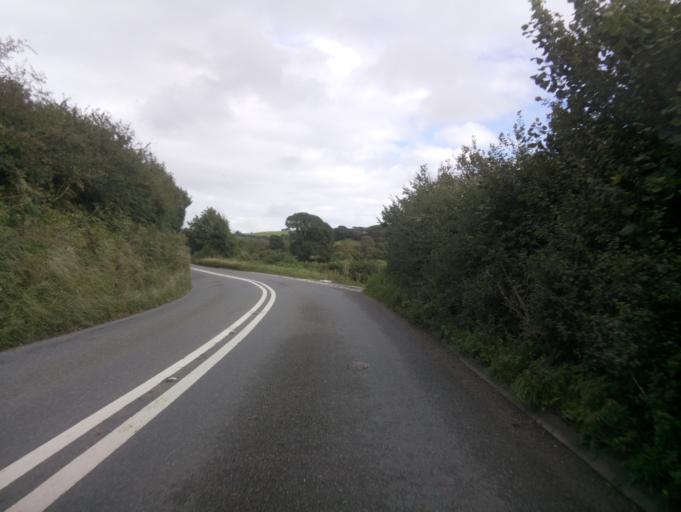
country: GB
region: England
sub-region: Devon
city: Modbury
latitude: 50.3451
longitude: -3.8856
